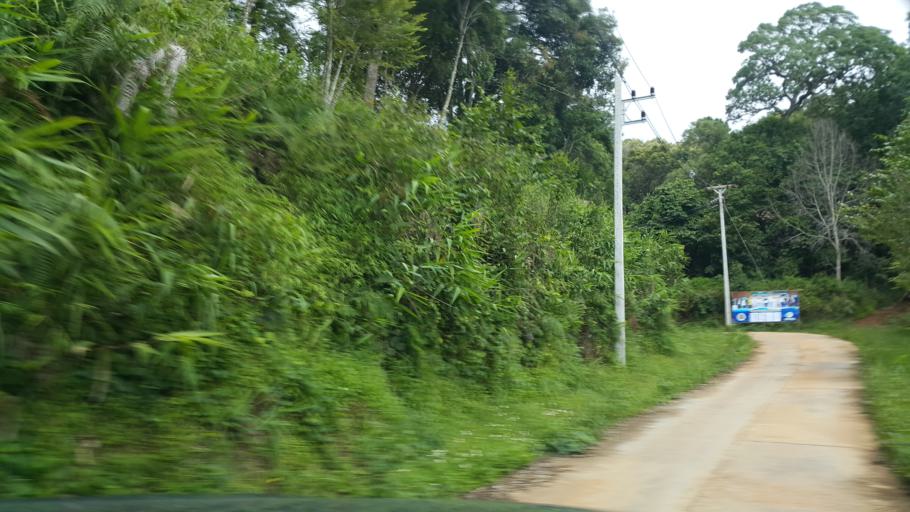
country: TH
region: Lampang
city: Wang Nuea
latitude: 19.1088
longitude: 99.3650
